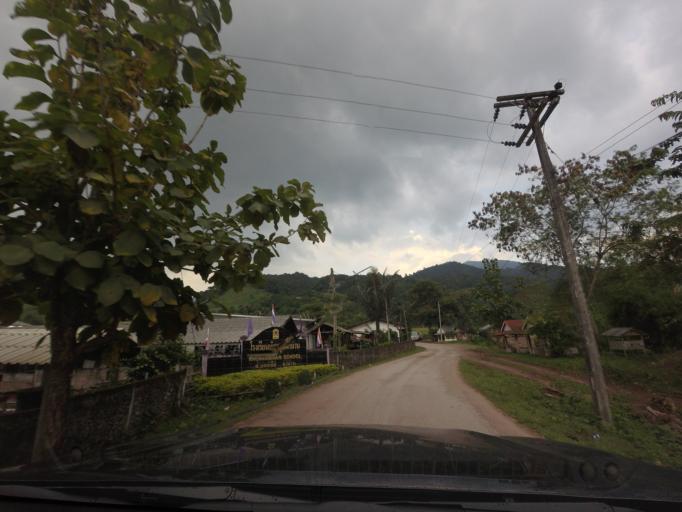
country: TH
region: Nan
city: Bo Kluea
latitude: 19.3516
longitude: 101.1587
